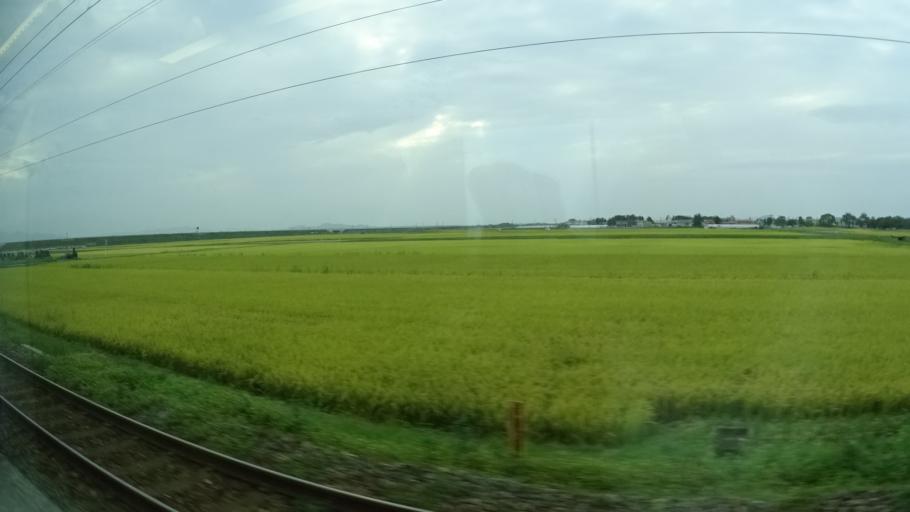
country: JP
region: Yamagata
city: Sakata
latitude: 38.8367
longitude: 139.9145
